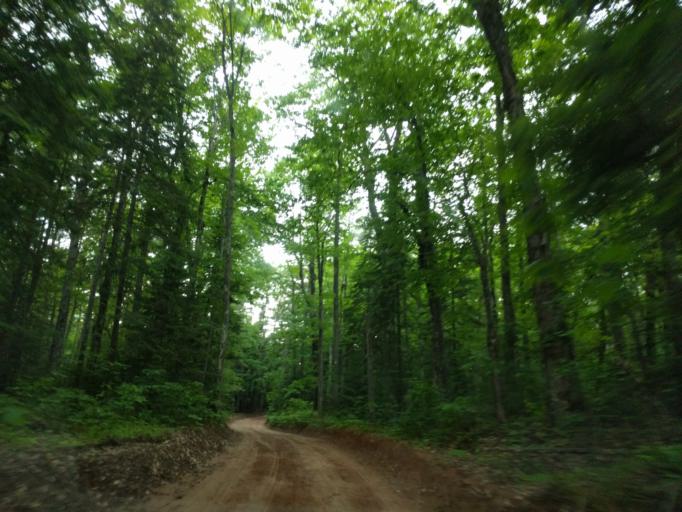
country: US
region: Michigan
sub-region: Marquette County
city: Trowbridge Park
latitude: 46.6024
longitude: -87.4986
